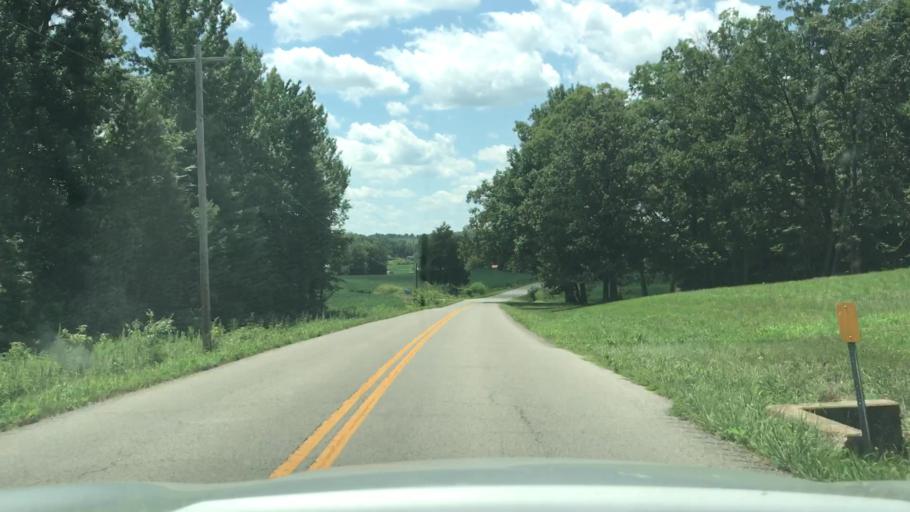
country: US
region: Kentucky
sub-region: Muhlenberg County
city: Greenville
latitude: 37.1360
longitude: -87.2690
